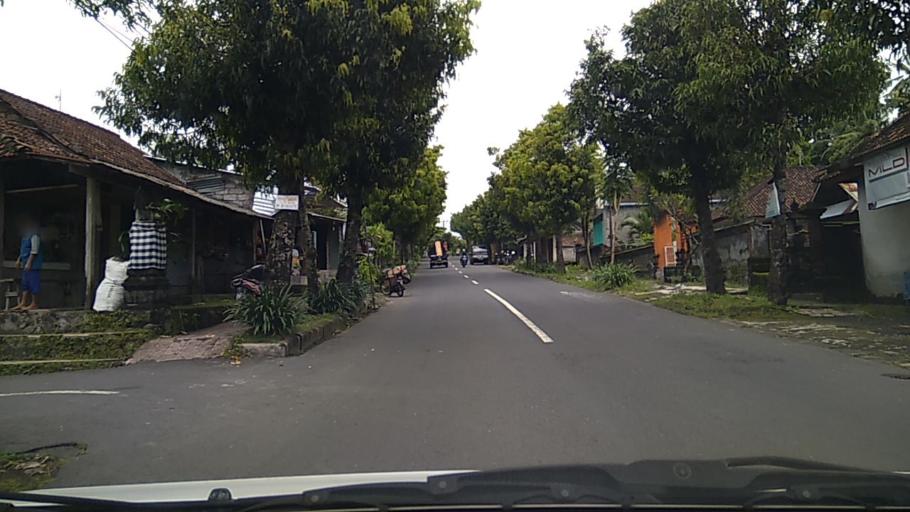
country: ID
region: Bali
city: Banjar Kelodan
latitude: -8.5311
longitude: 115.3484
